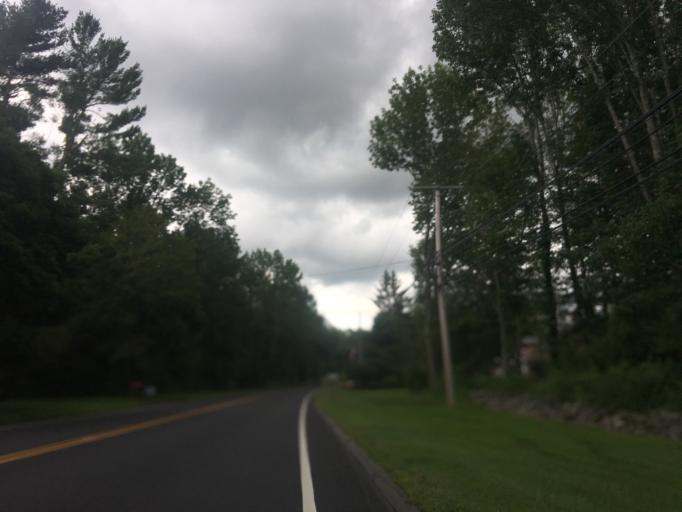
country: US
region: Connecticut
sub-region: Windham County
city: Wauregan
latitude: 41.7520
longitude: -71.9023
